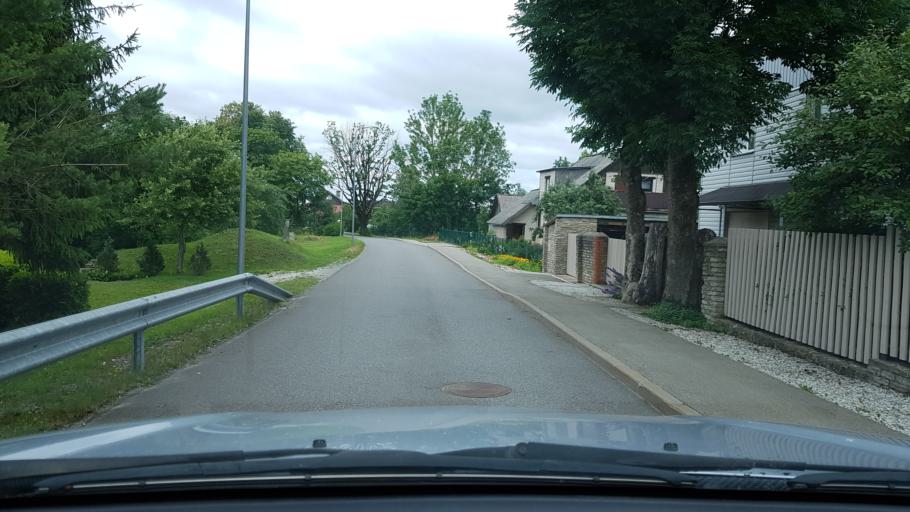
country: EE
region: Ida-Virumaa
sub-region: Narva linn
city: Narva
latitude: 59.3944
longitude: 28.1241
